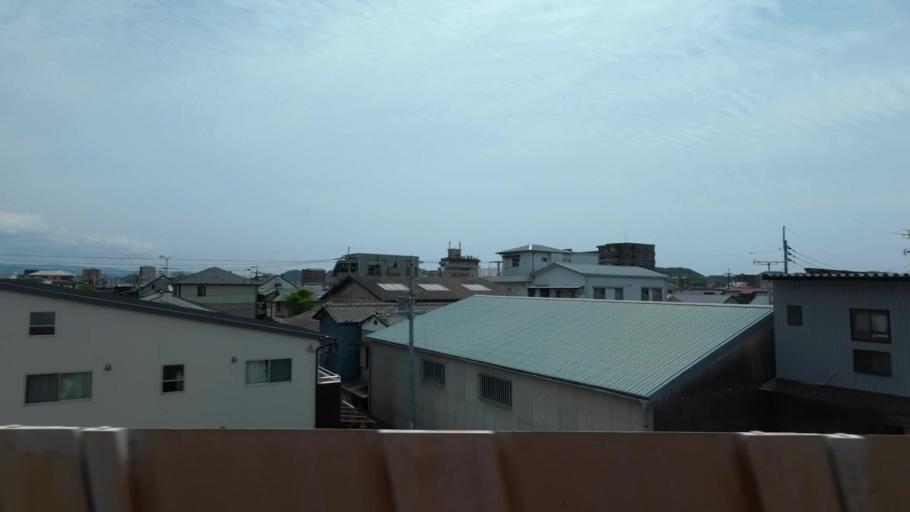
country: JP
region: Kochi
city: Kochi-shi
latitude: 33.5705
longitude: 133.5531
